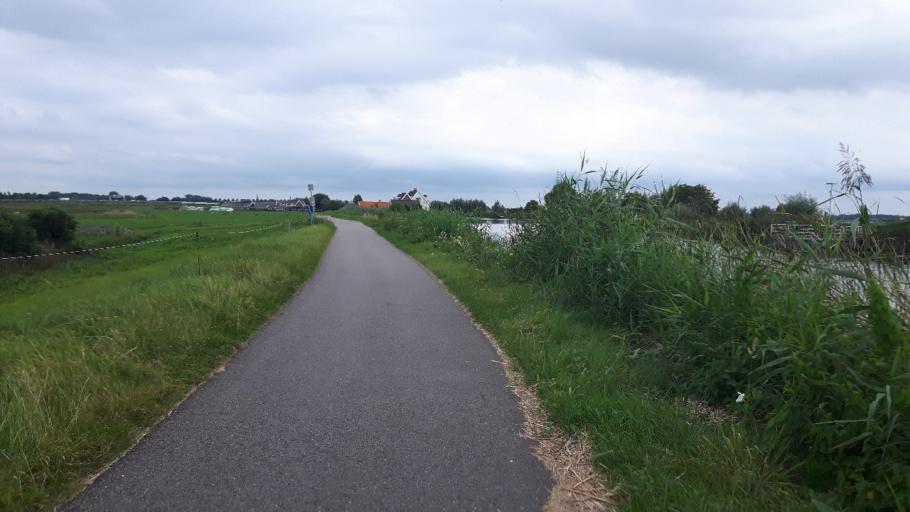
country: NL
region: North Holland
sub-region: Gemeente Ouder-Amstel
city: Ouderkerk aan de Amstel
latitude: 52.2807
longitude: 4.9351
